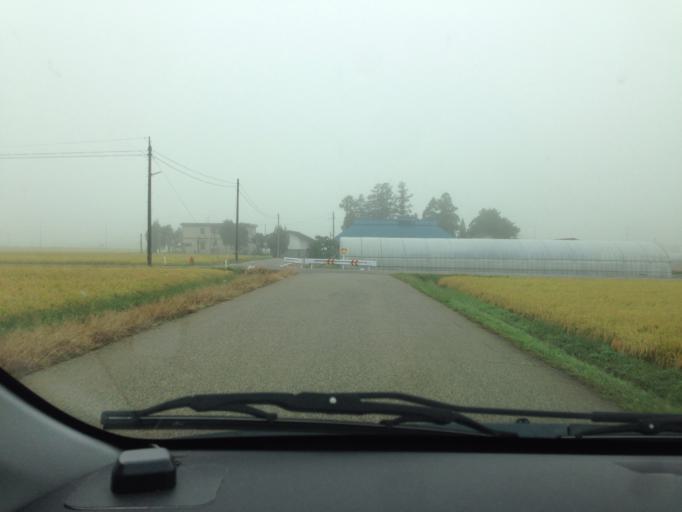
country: JP
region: Fukushima
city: Kitakata
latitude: 37.5579
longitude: 139.8666
